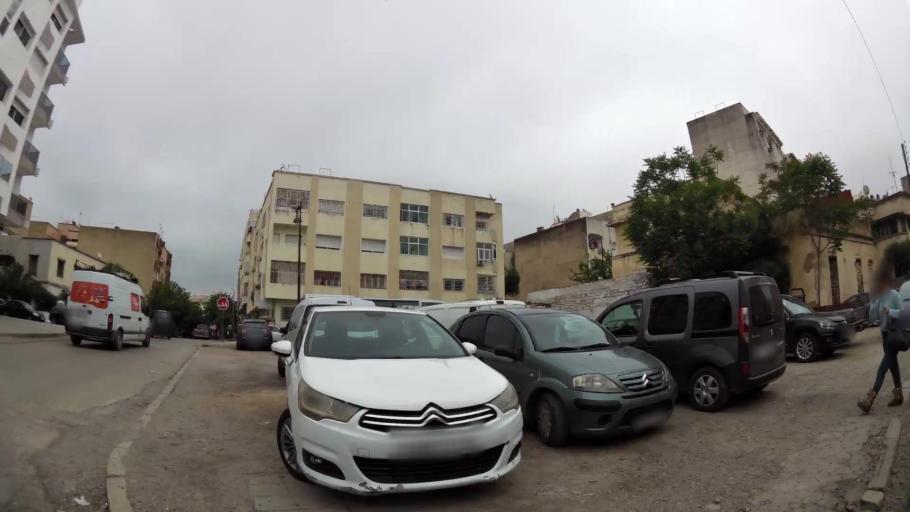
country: MA
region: Fes-Boulemane
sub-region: Fes
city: Fes
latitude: 34.0349
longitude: -4.9955
